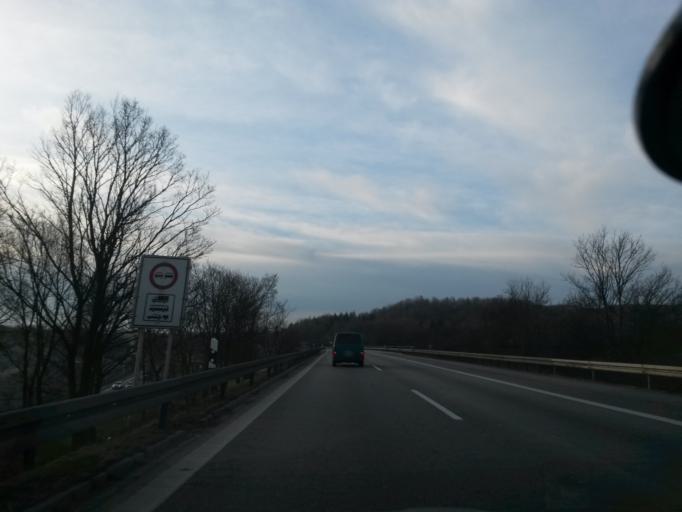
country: DE
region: Bavaria
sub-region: Upper Bavaria
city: Unterfoehring
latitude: 48.2204
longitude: 11.6327
